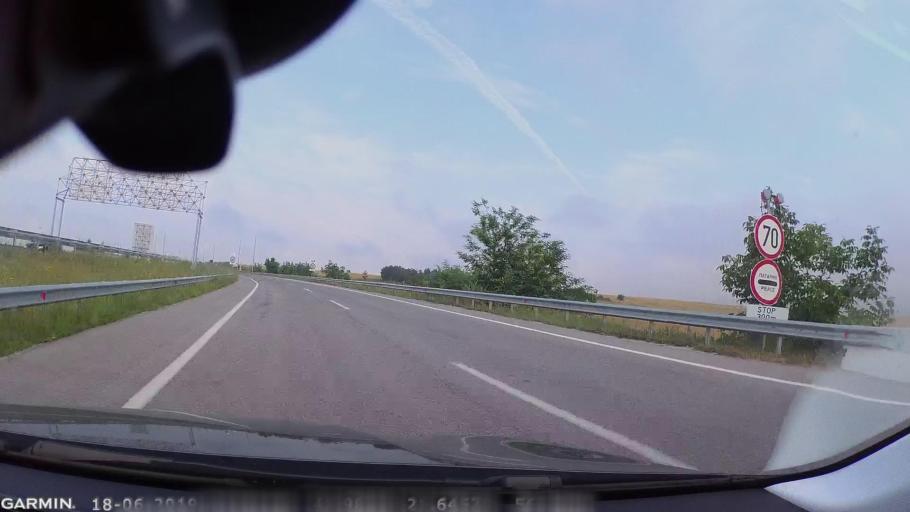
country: MK
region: Petrovec
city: Sredno Konjare
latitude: 41.9543
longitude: 21.7513
